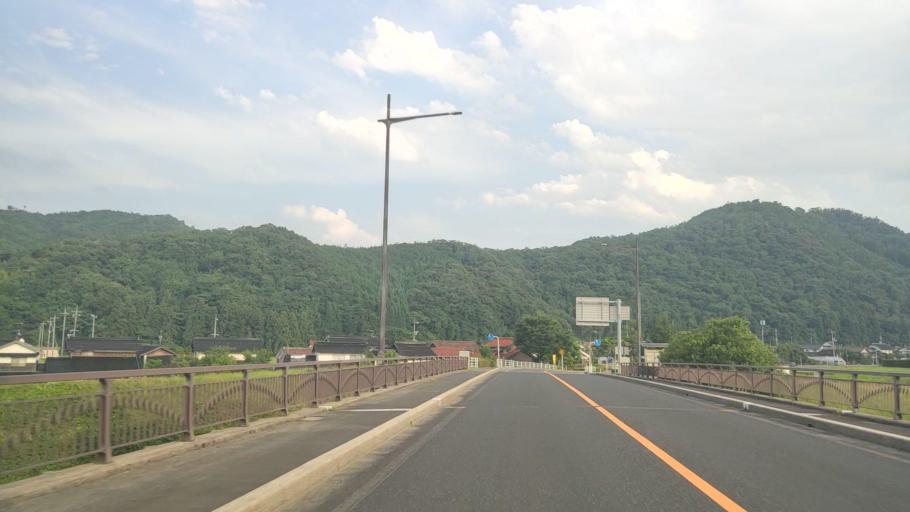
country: JP
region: Tottori
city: Kurayoshi
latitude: 35.3891
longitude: 133.7802
